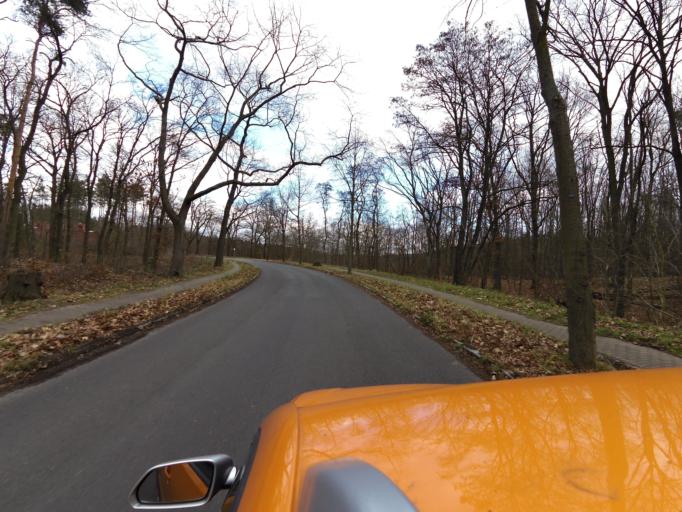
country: DE
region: Berlin
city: Gatow
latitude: 52.5002
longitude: 13.2221
